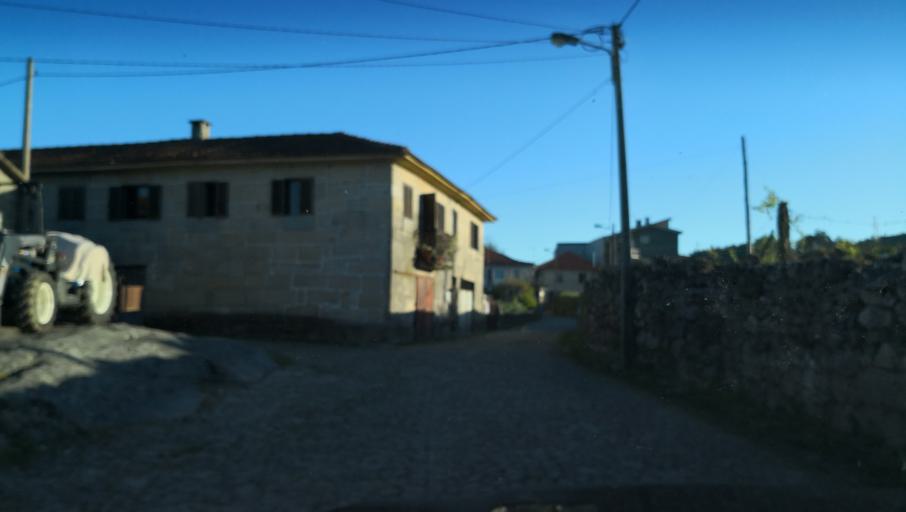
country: PT
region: Vila Real
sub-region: Sabrosa
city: Sabrosa
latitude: 41.3514
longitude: -7.6172
